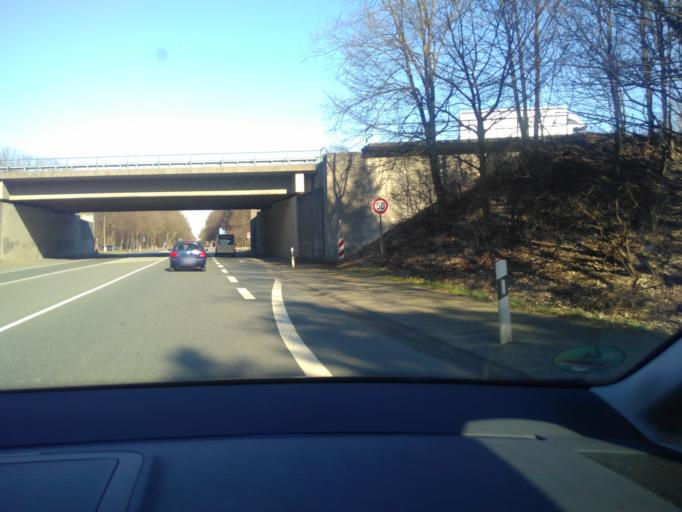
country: DE
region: North Rhine-Westphalia
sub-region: Regierungsbezirk Detmold
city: Rheda-Wiedenbruck
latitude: 51.8517
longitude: 8.3264
